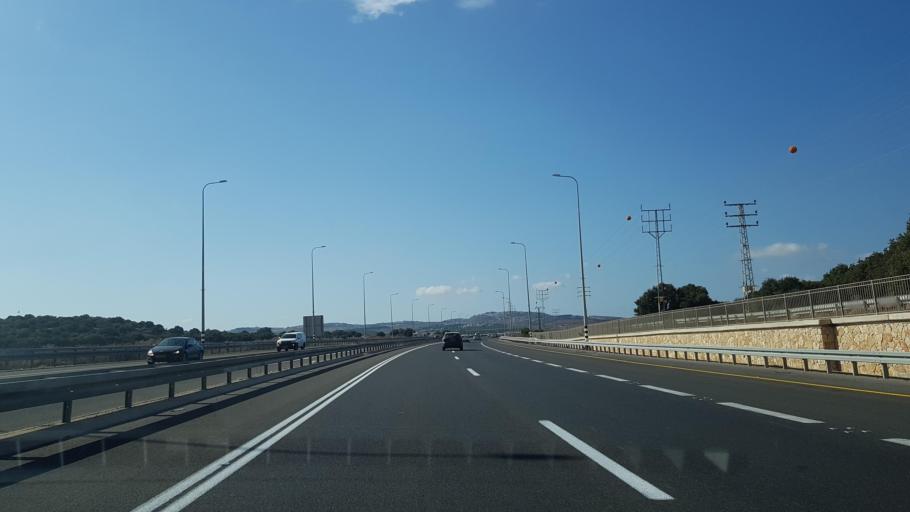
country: IL
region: Northern District
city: Rumat Heib
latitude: 32.7698
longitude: 35.2889
